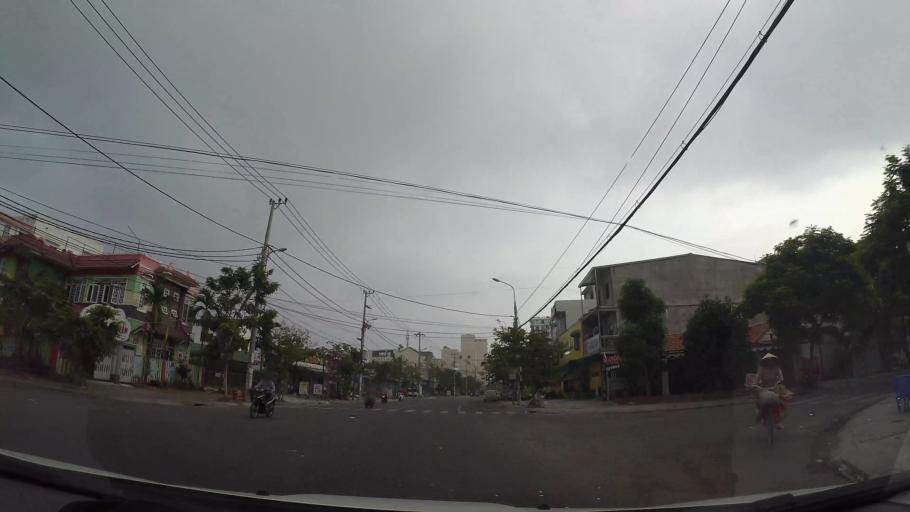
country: VN
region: Da Nang
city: Son Tra
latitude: 16.0820
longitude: 108.2442
